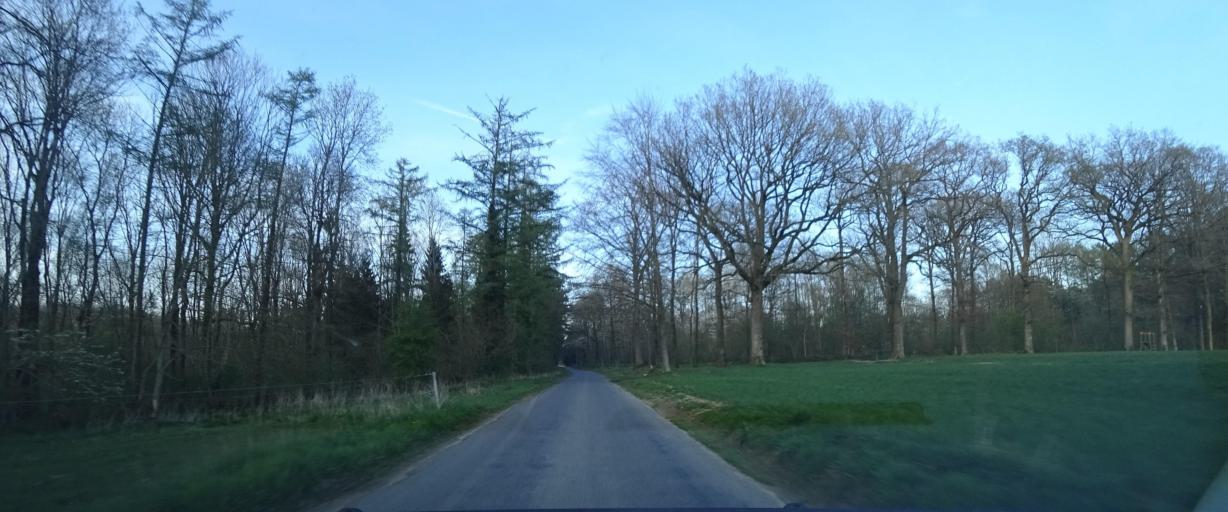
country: BE
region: Wallonia
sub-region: Province de Namur
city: Hamois
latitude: 50.3221
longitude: 5.2026
